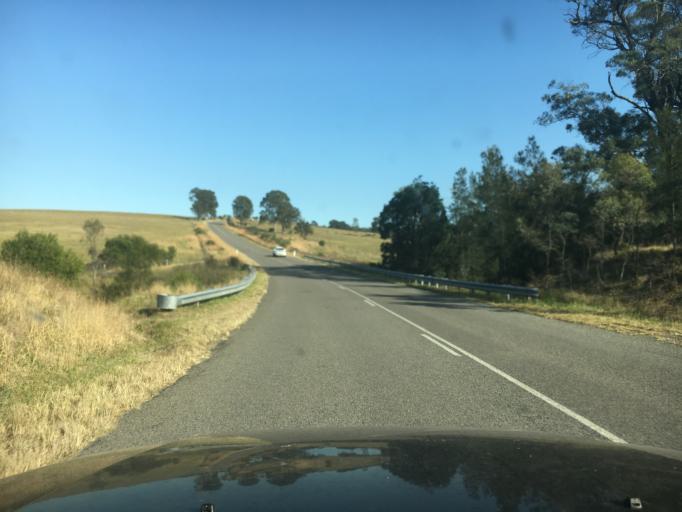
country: AU
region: New South Wales
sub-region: Cessnock
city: Branxton
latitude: -32.5840
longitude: 151.3267
